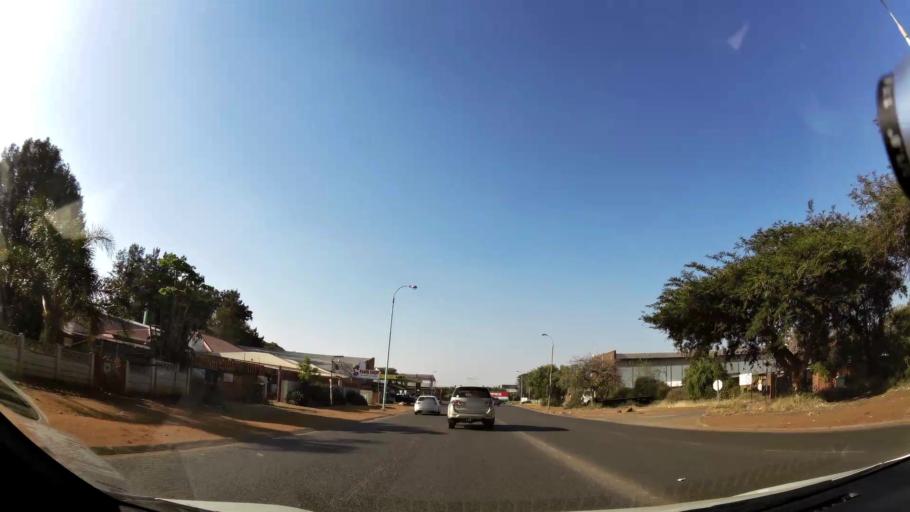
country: ZA
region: North-West
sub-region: Bojanala Platinum District Municipality
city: Rustenburg
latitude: -25.6719
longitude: 27.2530
